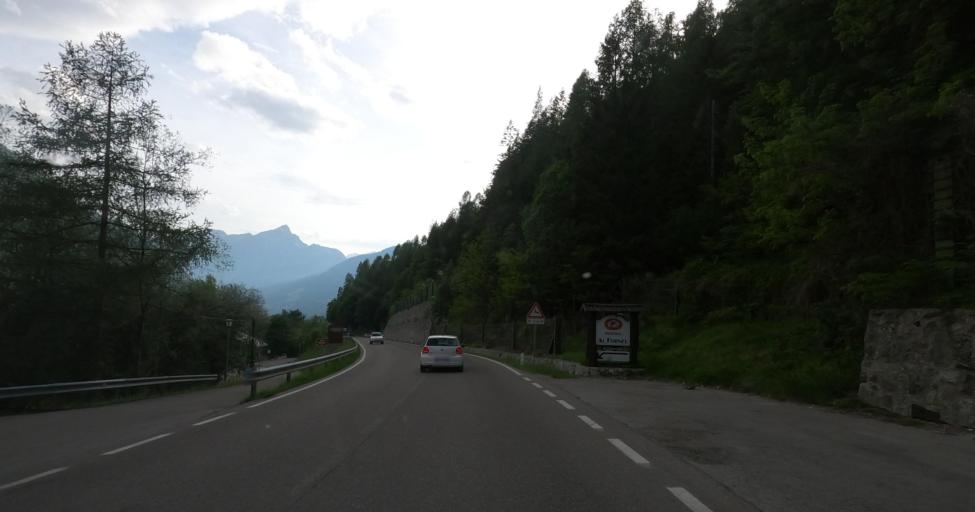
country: IT
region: Veneto
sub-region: Provincia di Belluno
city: Alleghe
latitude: 46.3957
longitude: 12.0069
